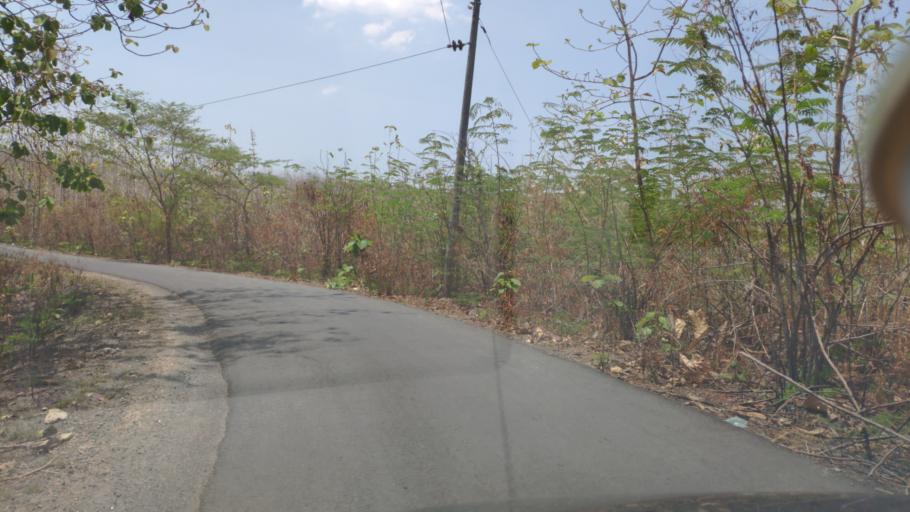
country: ID
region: Central Java
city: Randublatung
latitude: -7.2316
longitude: 111.3800
